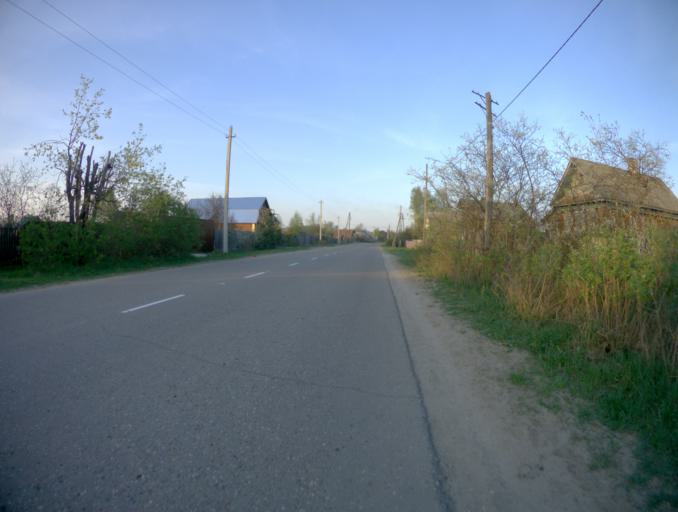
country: RU
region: Ivanovo
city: Yuzha
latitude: 56.5880
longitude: 42.0329
